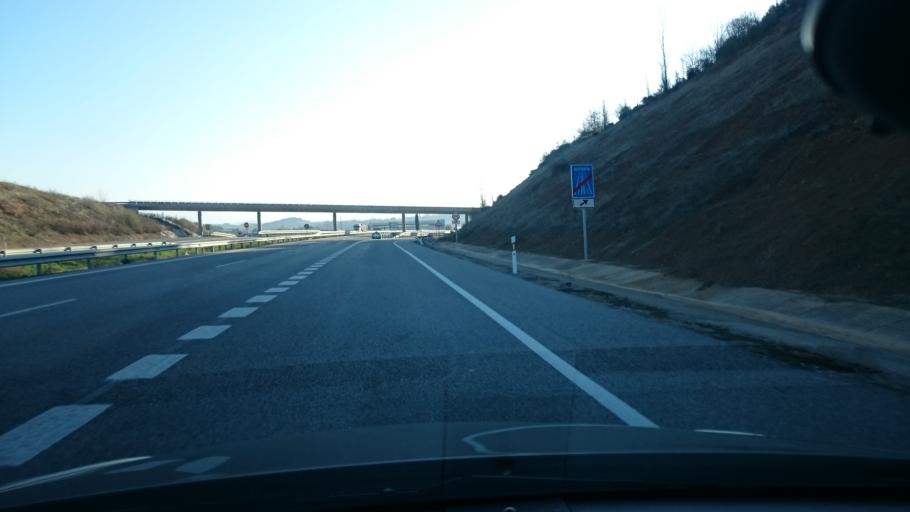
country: ES
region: Castille and Leon
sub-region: Provincia de Leon
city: Camponaraya
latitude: 42.5861
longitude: -6.6805
